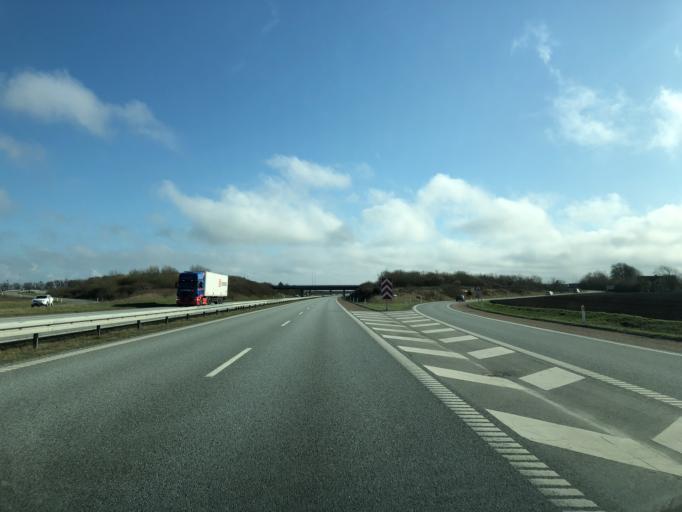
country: DK
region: North Denmark
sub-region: Hjorring Kommune
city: Hjorring
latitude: 57.4597
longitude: 10.0457
